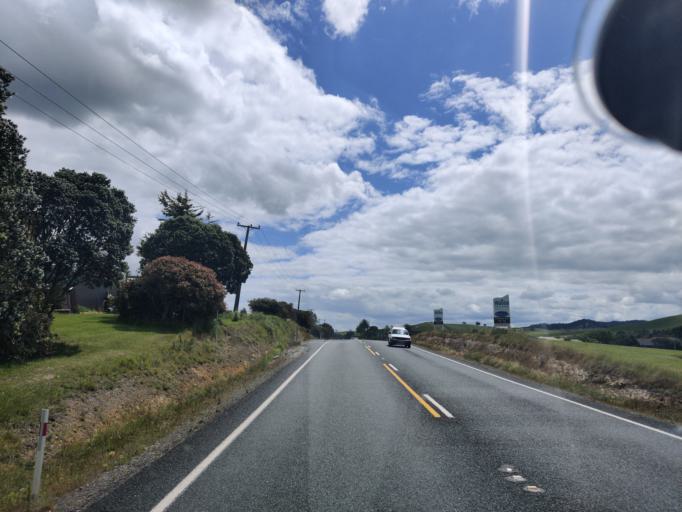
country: NZ
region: Northland
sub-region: Far North District
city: Paihia
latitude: -35.2809
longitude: 174.0478
